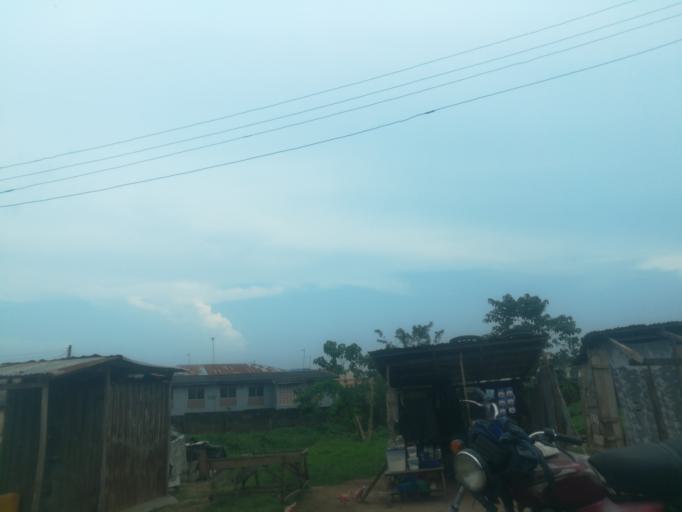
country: NG
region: Oyo
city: Ibadan
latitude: 7.3776
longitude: 3.8253
